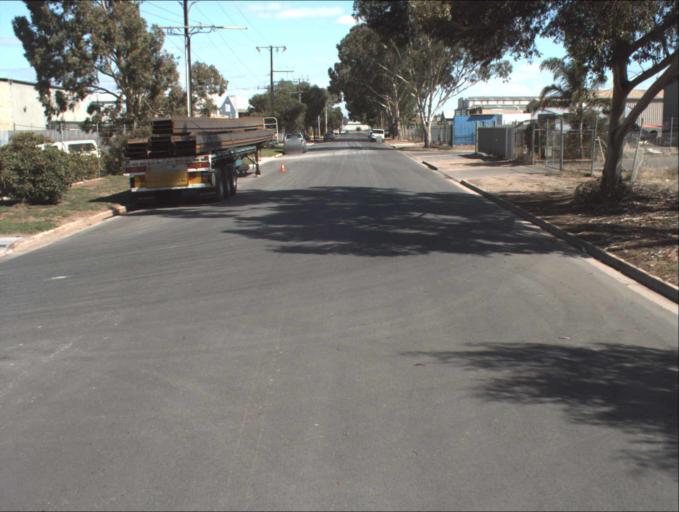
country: AU
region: South Australia
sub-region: Charles Sturt
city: Woodville North
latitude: -34.8343
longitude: 138.5590
